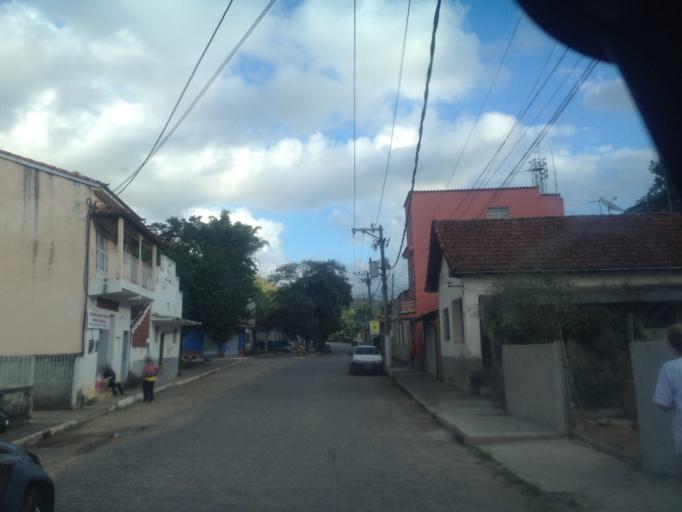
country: BR
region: Rio de Janeiro
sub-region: Quatis
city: Quatis
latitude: -22.2891
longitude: -44.2563
